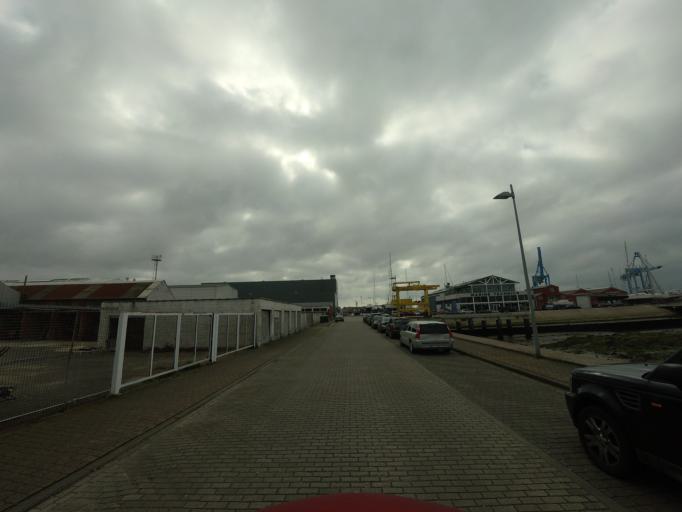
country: BE
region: Flanders
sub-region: Provincie West-Vlaanderen
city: Zeebrugge
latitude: 51.3301
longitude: 3.2008
